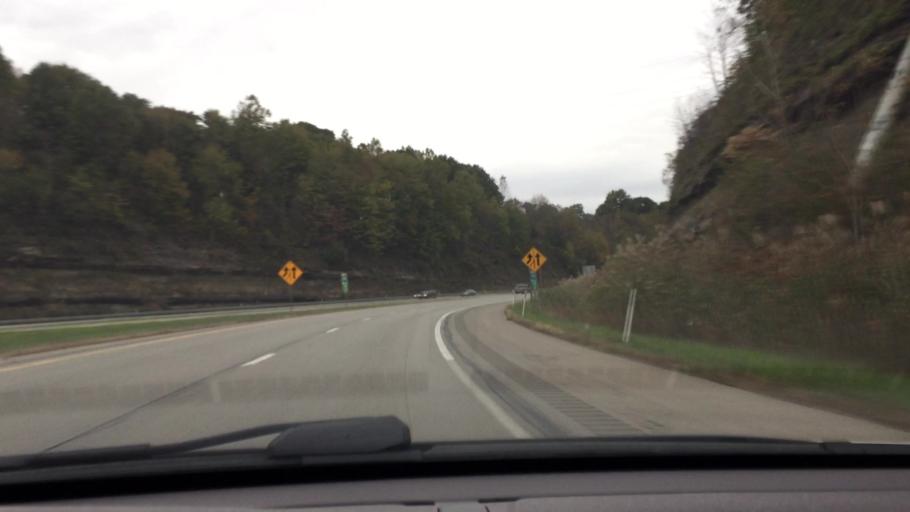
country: US
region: Pennsylvania
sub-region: Lawrence County
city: Oakwood
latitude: 40.9993
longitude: -80.3923
